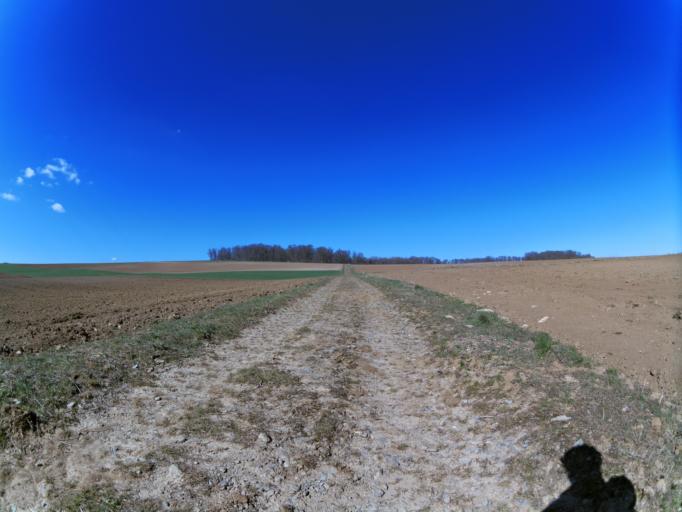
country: DE
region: Bavaria
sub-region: Regierungsbezirk Unterfranken
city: Hettstadt
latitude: 49.8005
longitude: 9.7912
